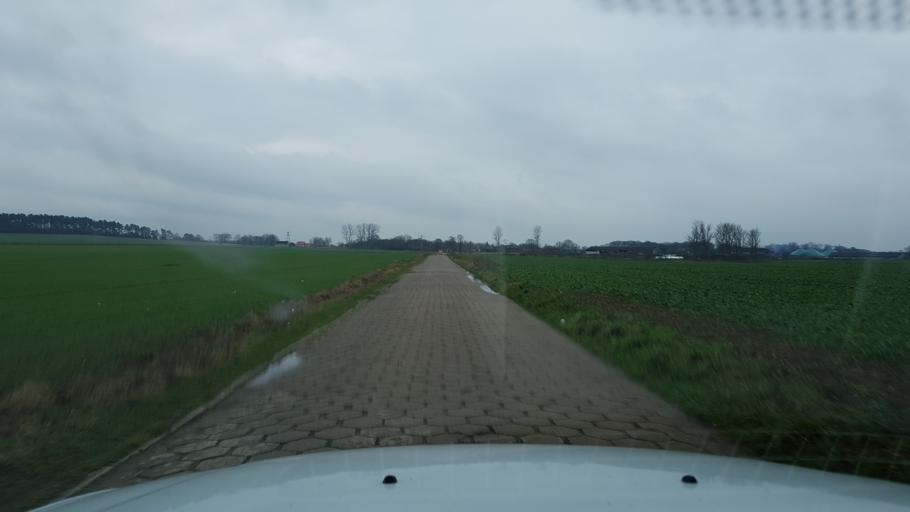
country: PL
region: West Pomeranian Voivodeship
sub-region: Powiat kolobrzeski
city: Grzybowo
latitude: 54.1016
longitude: 15.4465
